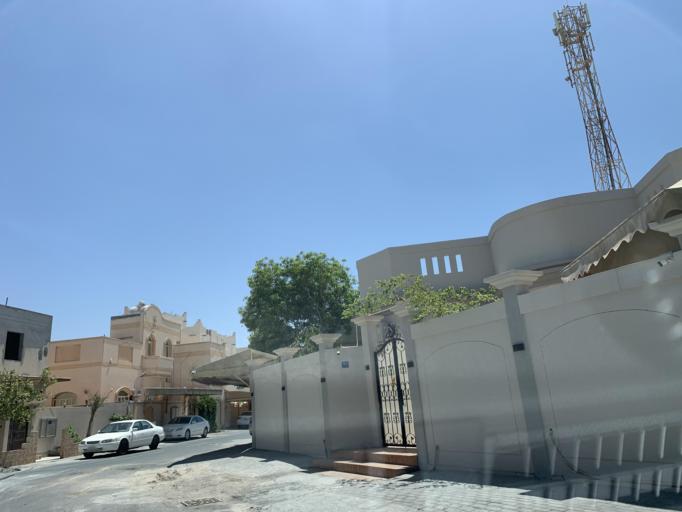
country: BH
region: Manama
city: Jidd Hafs
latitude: 26.2304
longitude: 50.4871
